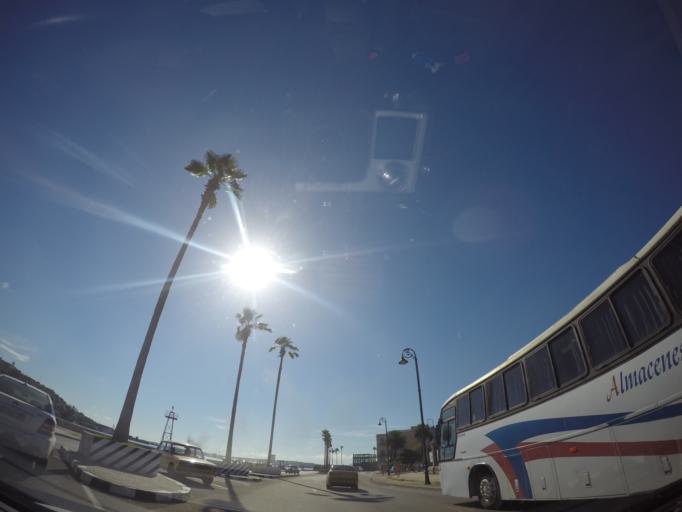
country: CU
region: La Habana
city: La Habana Vieja
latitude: 23.1418
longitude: -82.3495
